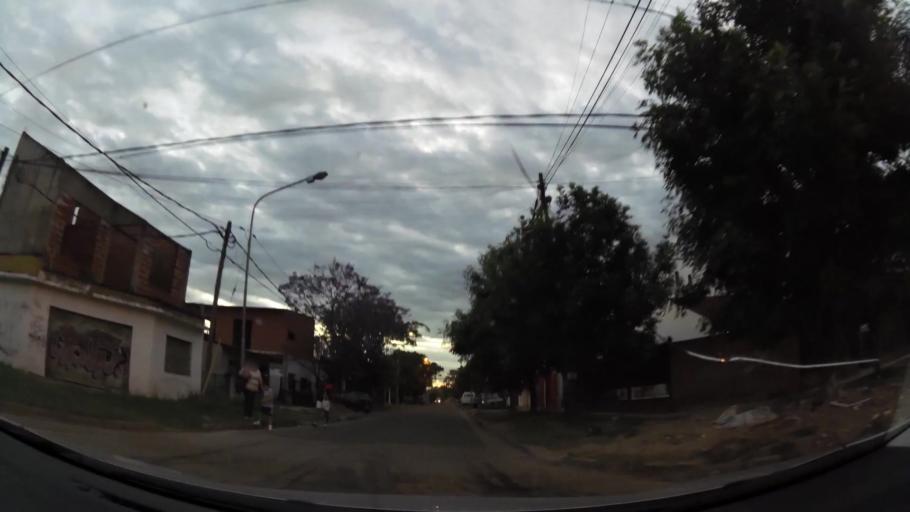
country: AR
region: Buenos Aires
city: Santa Catalina - Dique Lujan
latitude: -34.4150
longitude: -58.6882
